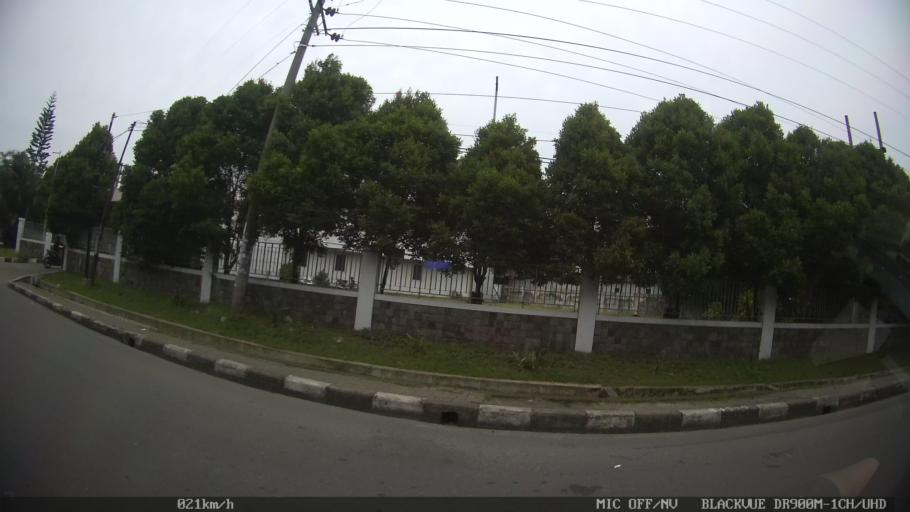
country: ID
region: North Sumatra
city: Deli Tua
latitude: 3.5359
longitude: 98.7211
